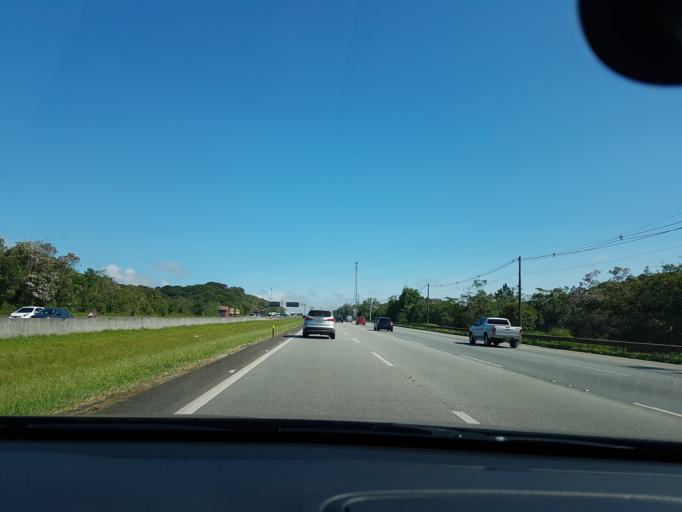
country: BR
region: Sao Paulo
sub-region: Cubatao
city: Cubatao
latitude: -23.8796
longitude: -46.5689
